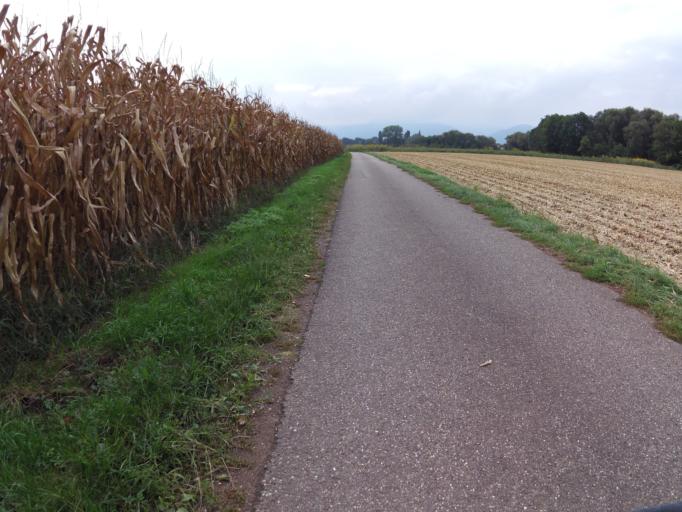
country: FR
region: Alsace
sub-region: Departement du Haut-Rhin
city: Guemar
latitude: 48.1867
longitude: 7.4105
